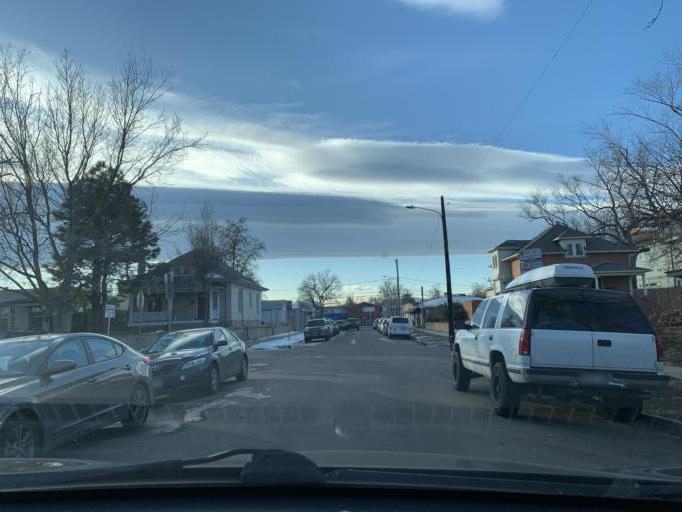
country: US
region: Colorado
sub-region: Jefferson County
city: Edgewater
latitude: 39.7725
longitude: -105.0425
